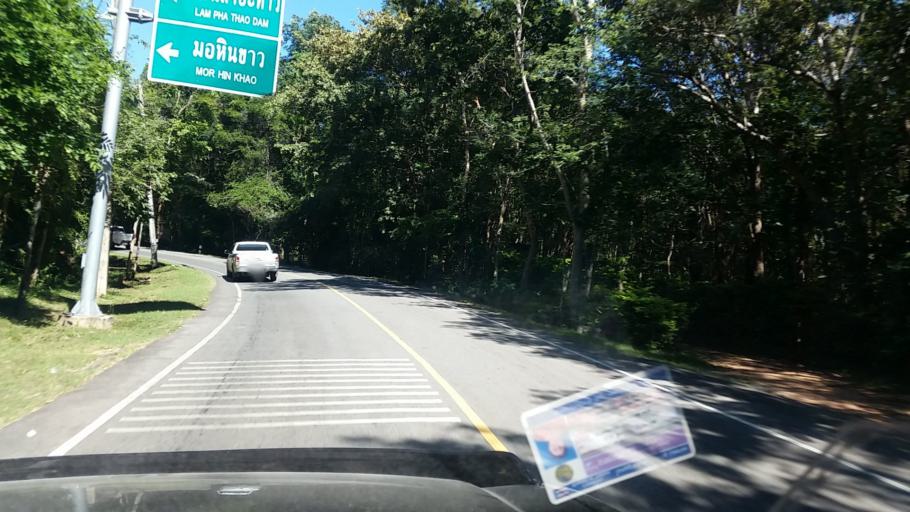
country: TH
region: Chaiyaphum
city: Chaiyaphum
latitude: 15.9748
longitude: 102.0268
